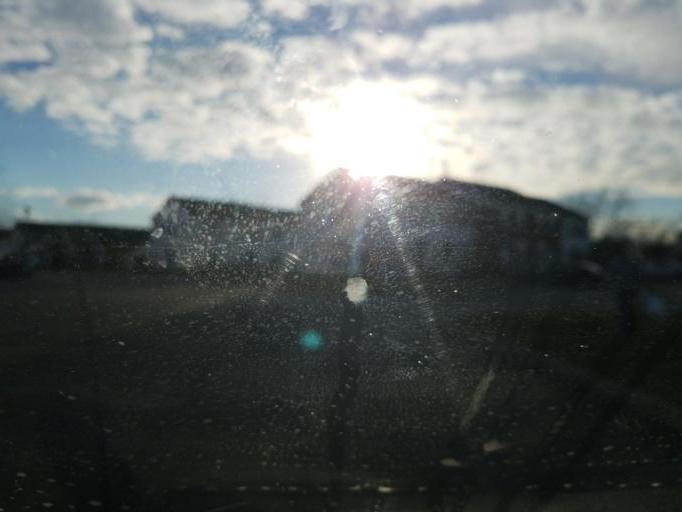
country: US
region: Ohio
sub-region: Delaware County
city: Delaware
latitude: 40.3187
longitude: -83.1101
